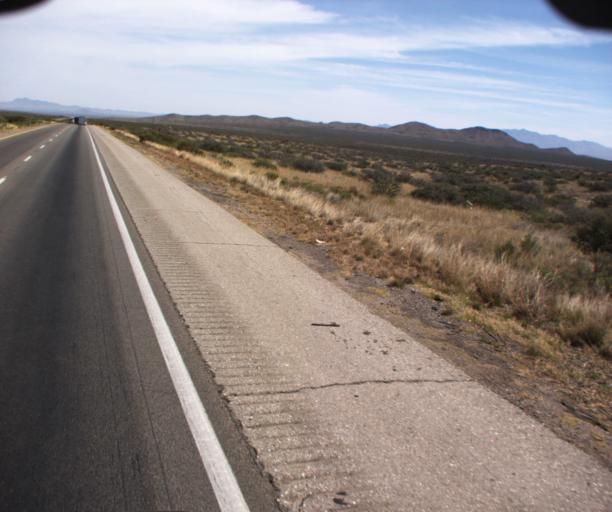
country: US
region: Arizona
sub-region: Cochise County
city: Willcox
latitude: 32.1143
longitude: -110.0211
